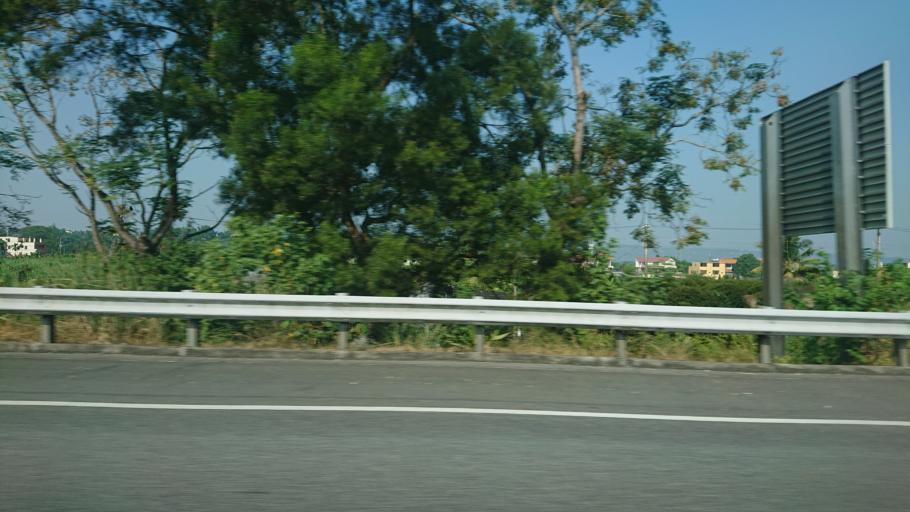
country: TW
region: Taiwan
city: Lugu
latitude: 23.7808
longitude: 120.7019
